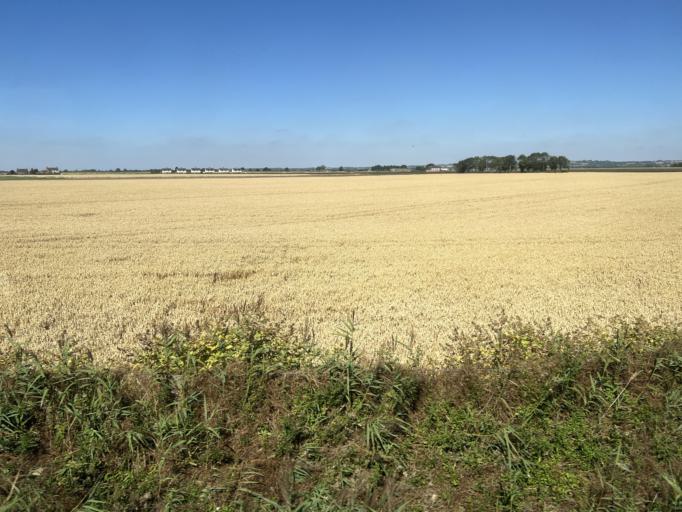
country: GB
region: England
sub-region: Lincolnshire
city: Spilsby
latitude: 53.0960
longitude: 0.1049
